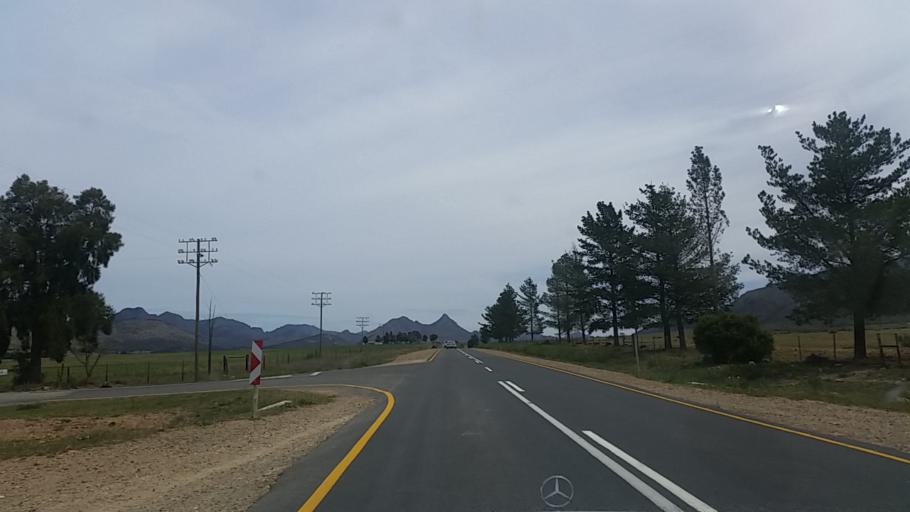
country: ZA
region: Western Cape
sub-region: Eden District Municipality
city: George
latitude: -33.8174
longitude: 22.5087
